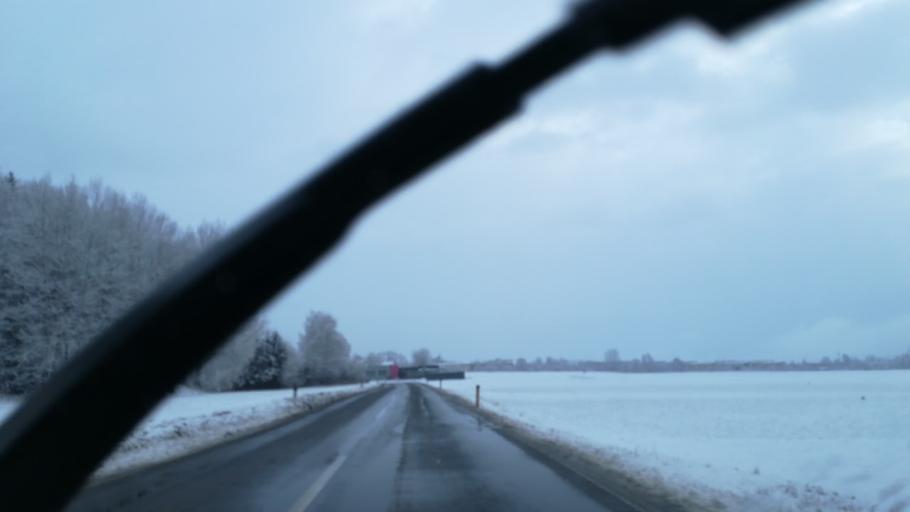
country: AT
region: Styria
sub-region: Politischer Bezirk Murtal
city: Fohnsdorf
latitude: 47.2057
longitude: 14.6520
